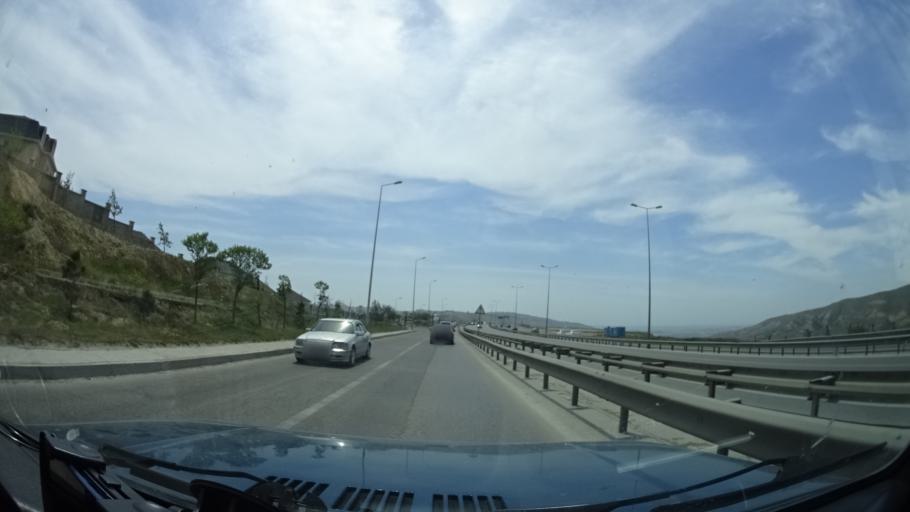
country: AZ
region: Baki
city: Badamdar
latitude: 40.3769
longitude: 49.7901
